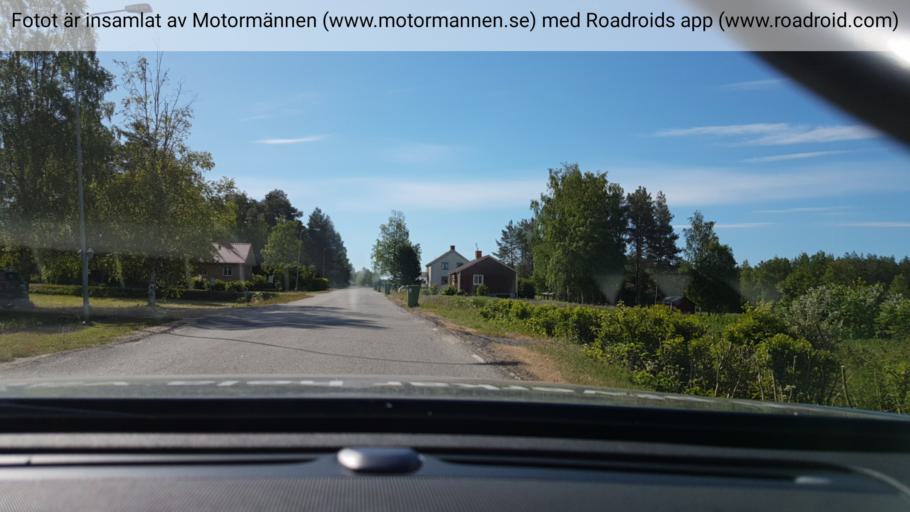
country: SE
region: Vaesterbotten
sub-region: Bjurholms Kommun
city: Bjurholm
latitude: 64.1199
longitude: 19.3111
